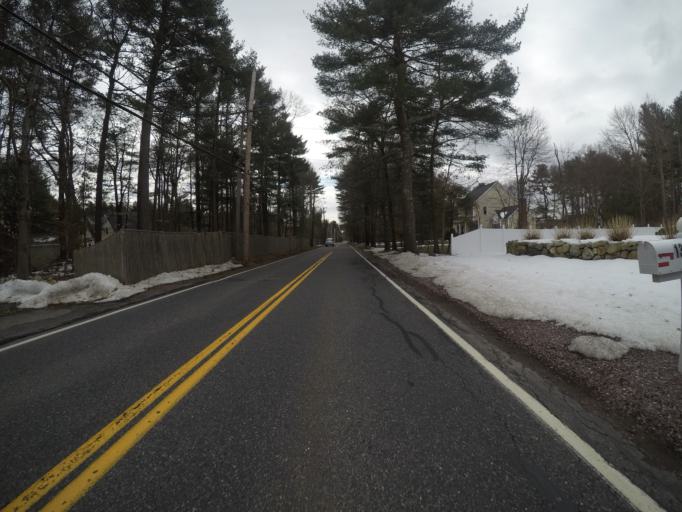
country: US
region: Massachusetts
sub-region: Bristol County
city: Easton
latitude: 42.0574
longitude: -71.1312
